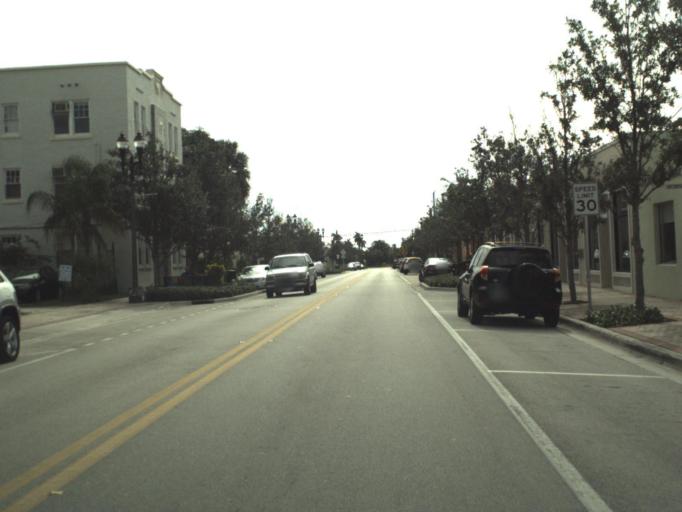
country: US
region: Florida
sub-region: Palm Beach County
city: West Palm Beach
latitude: 26.7357
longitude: -80.0564
